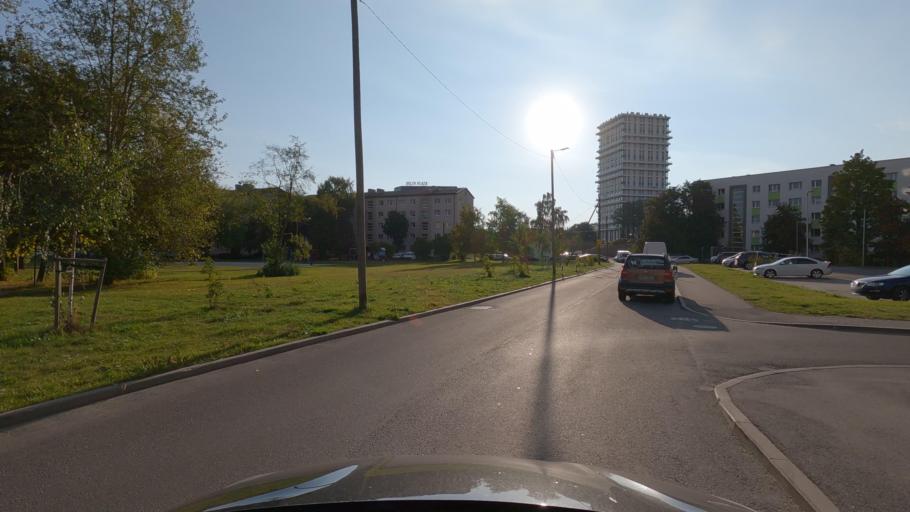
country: EE
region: Harju
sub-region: Tallinna linn
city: Tallinn
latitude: 59.4036
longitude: 24.7234
